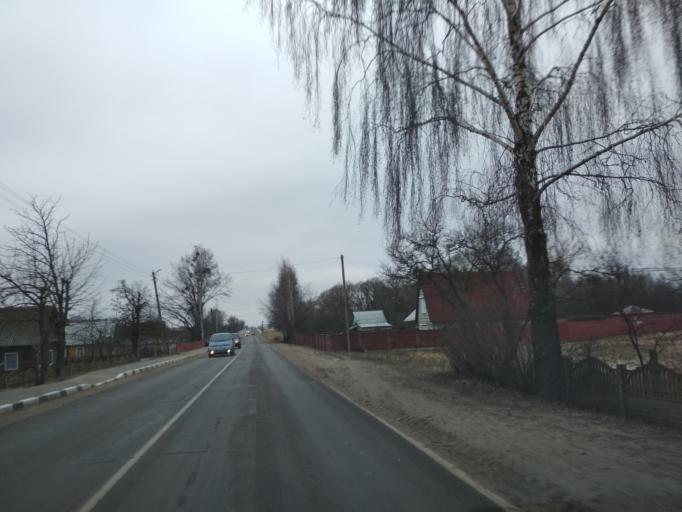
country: BY
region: Minsk
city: Mar''ina Horka
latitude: 53.5003
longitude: 28.1471
